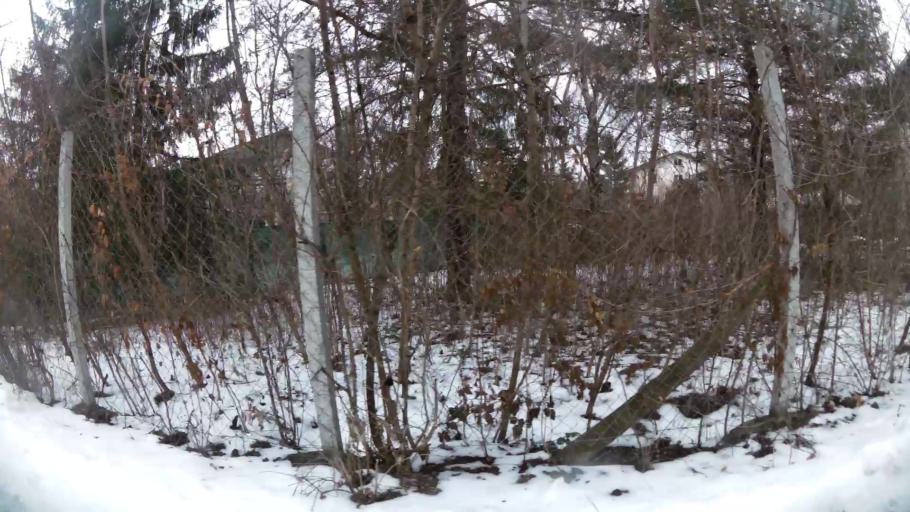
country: BG
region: Sofiya
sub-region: Obshtina Bozhurishte
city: Bozhurishte
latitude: 42.6731
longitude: 23.2346
